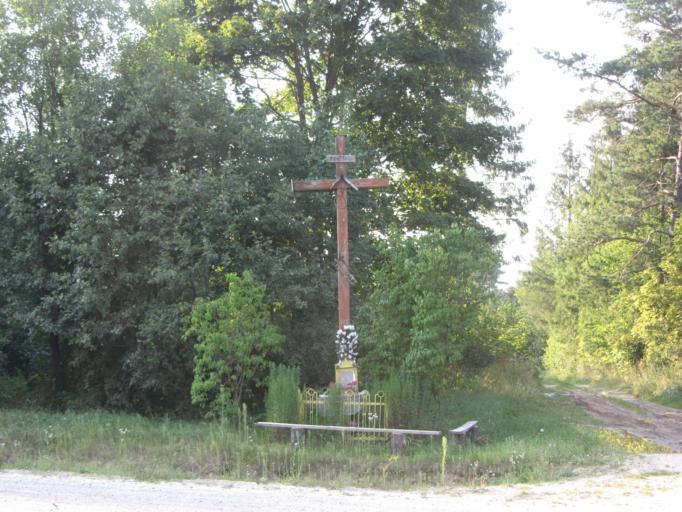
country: BY
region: Grodnenskaya
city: Astravyets
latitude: 54.6036
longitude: 25.6756
